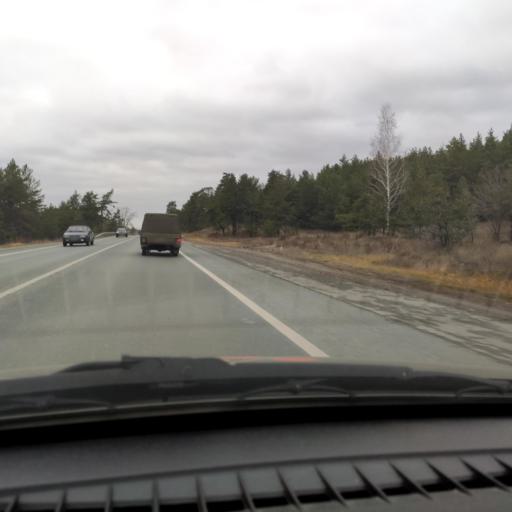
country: RU
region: Samara
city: Volzhskiy
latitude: 53.4437
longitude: 50.1030
